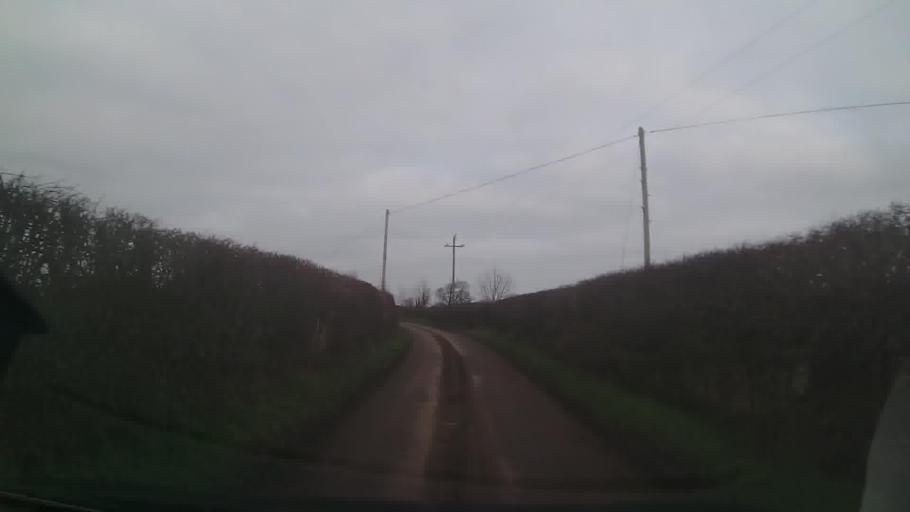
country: GB
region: England
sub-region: Shropshire
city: Petton
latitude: 52.8286
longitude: -2.7895
